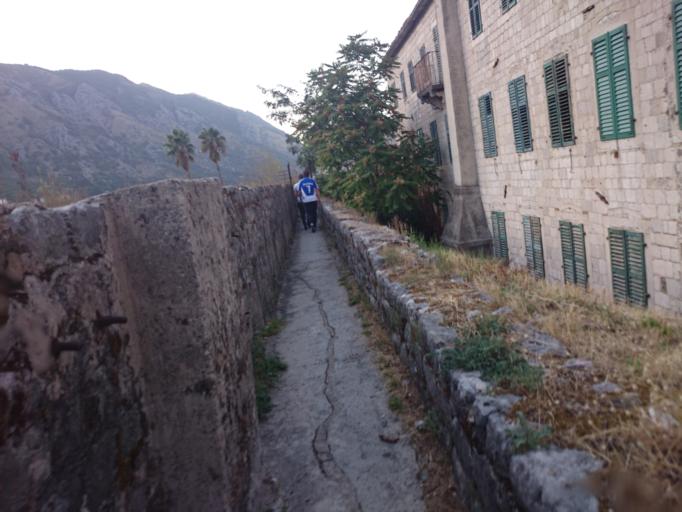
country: ME
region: Kotor
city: Kotor
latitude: 42.4243
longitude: 18.7703
